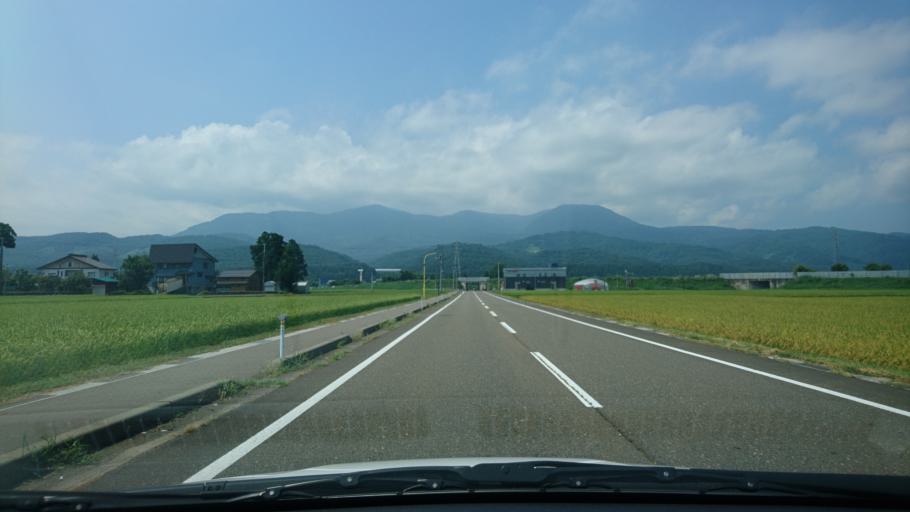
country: JP
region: Niigata
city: Arai
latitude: 37.0511
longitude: 138.2512
